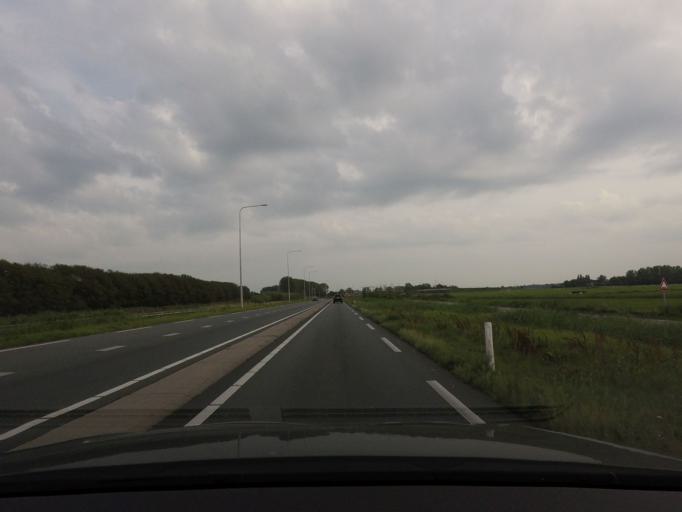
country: NL
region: North Holland
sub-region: Gemeente Schagen
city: Harenkarspel
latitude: 52.7137
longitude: 4.7106
